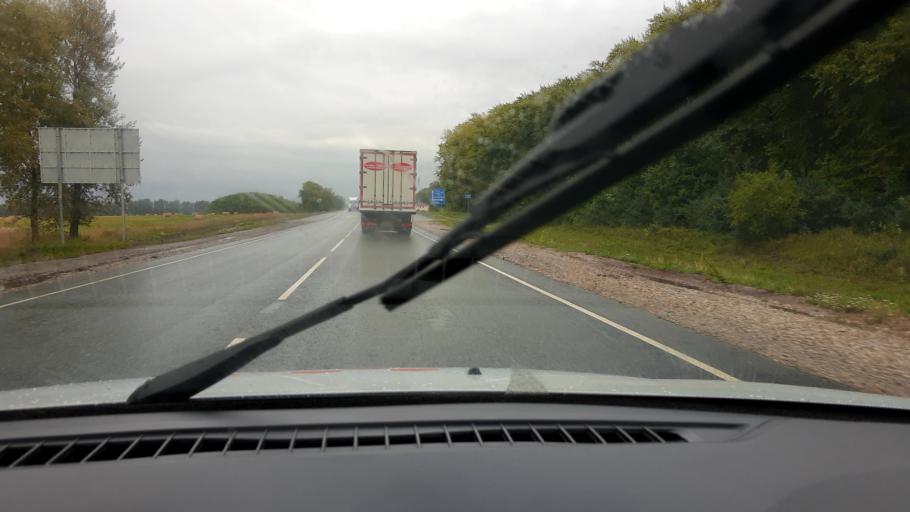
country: RU
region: Chuvashia
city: Yantikovo
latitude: 55.7890
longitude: 47.7237
